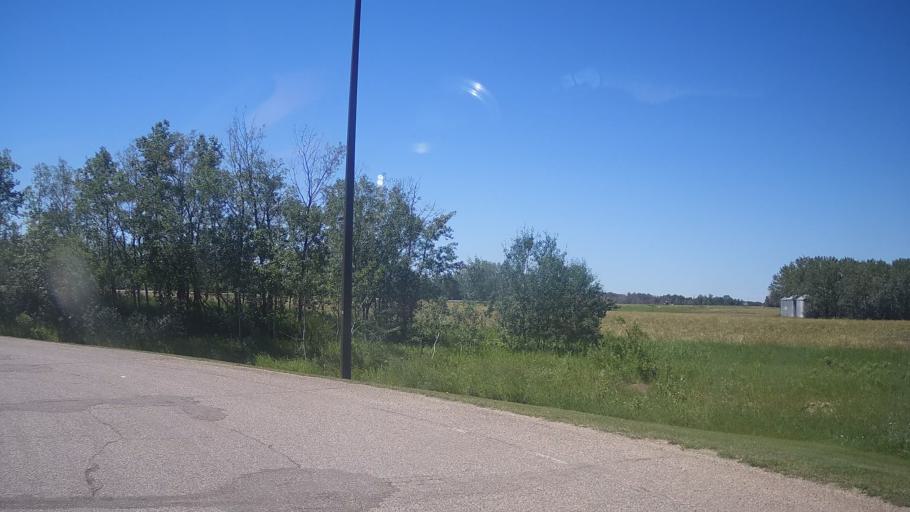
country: CA
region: Manitoba
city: Minnedosa
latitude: 50.2711
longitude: -99.9074
